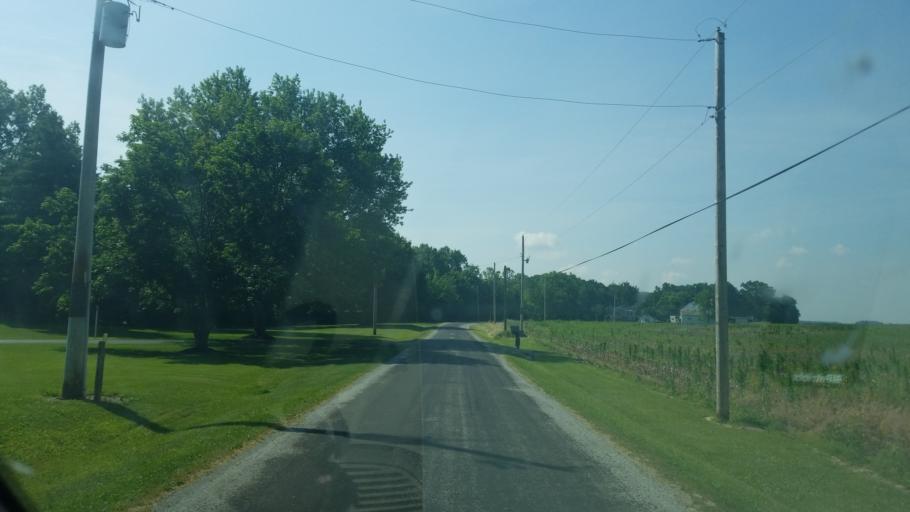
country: US
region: Ohio
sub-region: Wyandot County
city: Upper Sandusky
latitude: 40.9094
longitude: -83.2569
